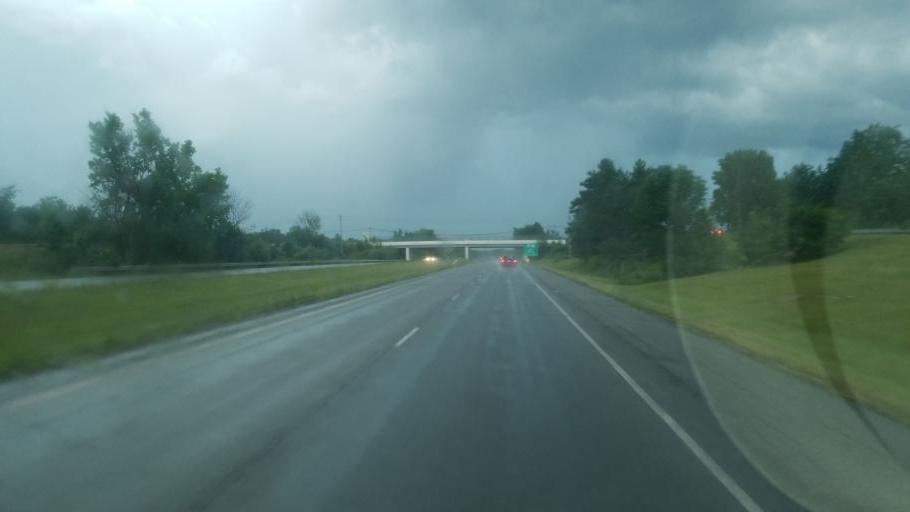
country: US
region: Ohio
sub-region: Summit County
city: Norton
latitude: 41.0518
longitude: -81.6623
